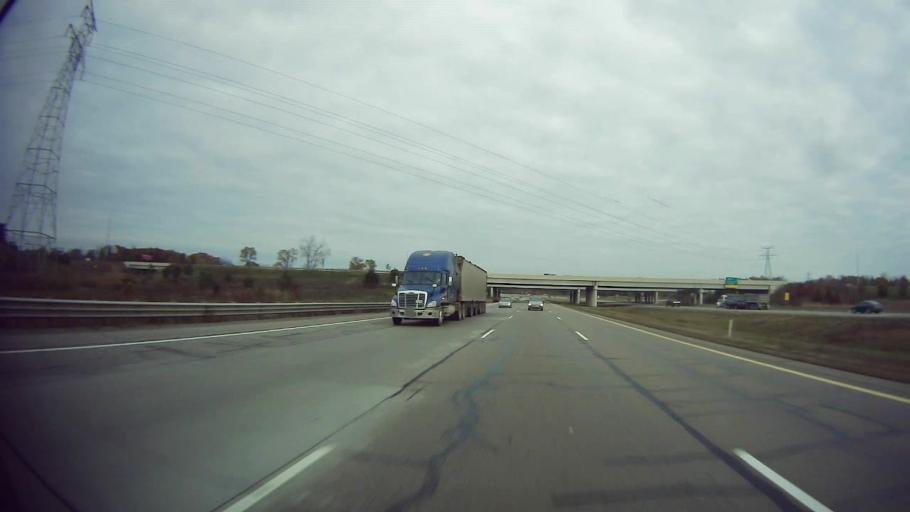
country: US
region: Michigan
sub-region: Wayne County
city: Romulus
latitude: 42.2208
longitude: -83.4124
